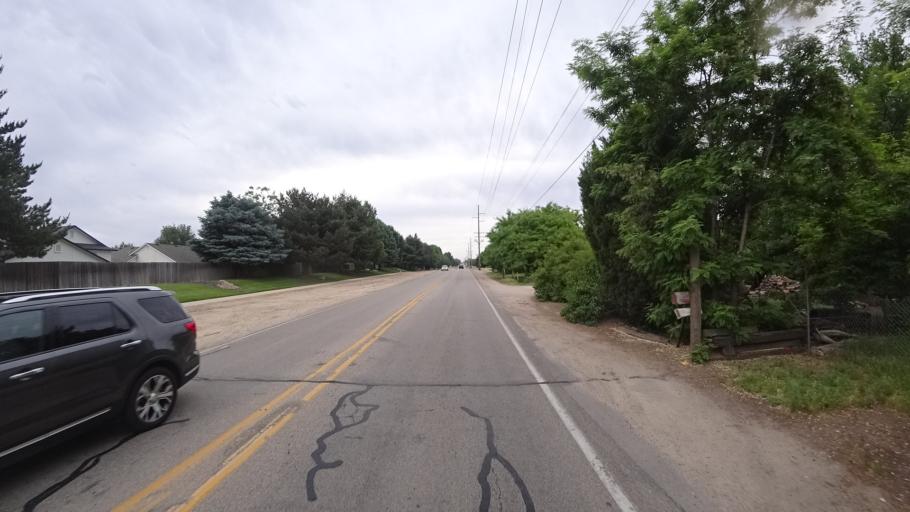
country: US
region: Idaho
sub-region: Ada County
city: Meridian
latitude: 43.5886
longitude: -116.3344
